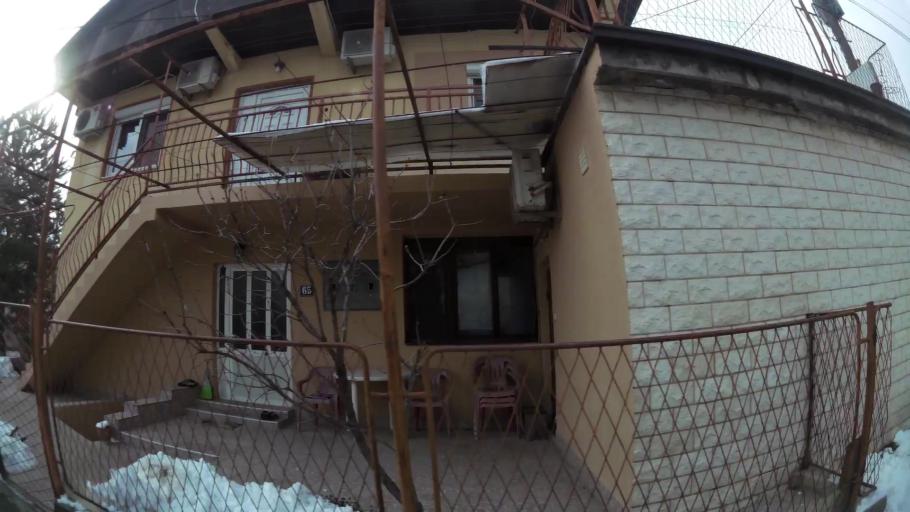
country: MK
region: Saraj
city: Saraj
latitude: 42.0214
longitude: 21.3544
